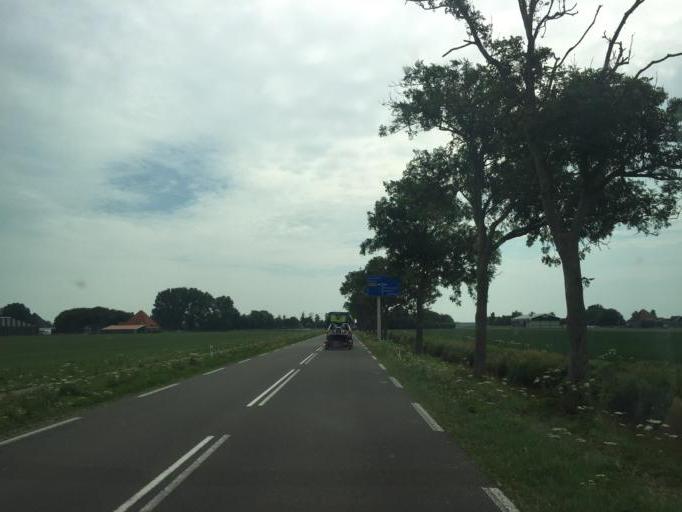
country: NL
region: North Holland
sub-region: Gemeente Beemster
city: Halfweg
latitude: 52.5890
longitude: 4.9311
